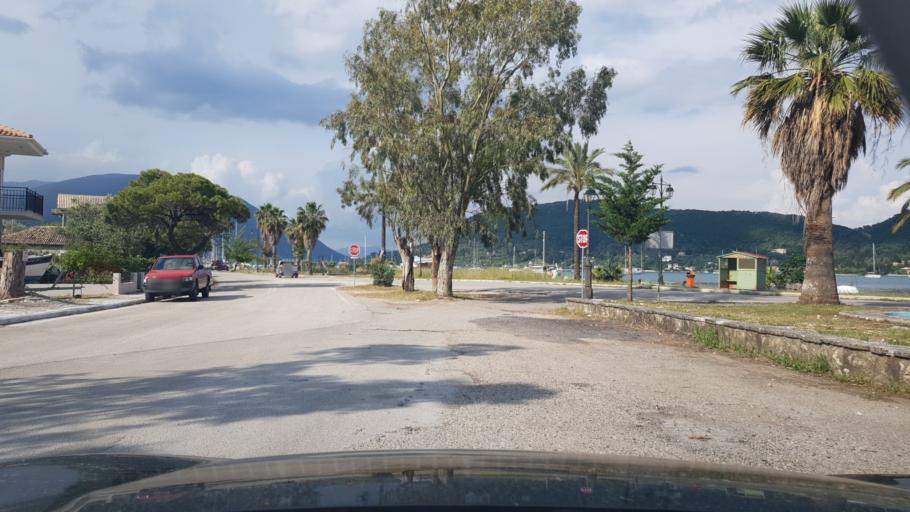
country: GR
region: Ionian Islands
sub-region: Lefkada
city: Nidri
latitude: 38.6803
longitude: 20.6977
